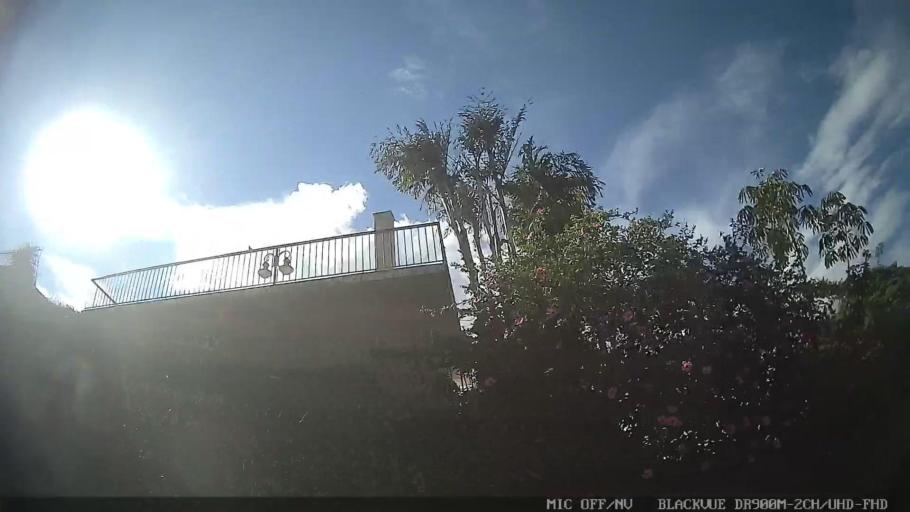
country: BR
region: Sao Paulo
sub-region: Serra Negra
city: Serra Negra
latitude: -22.6125
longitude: -46.7068
